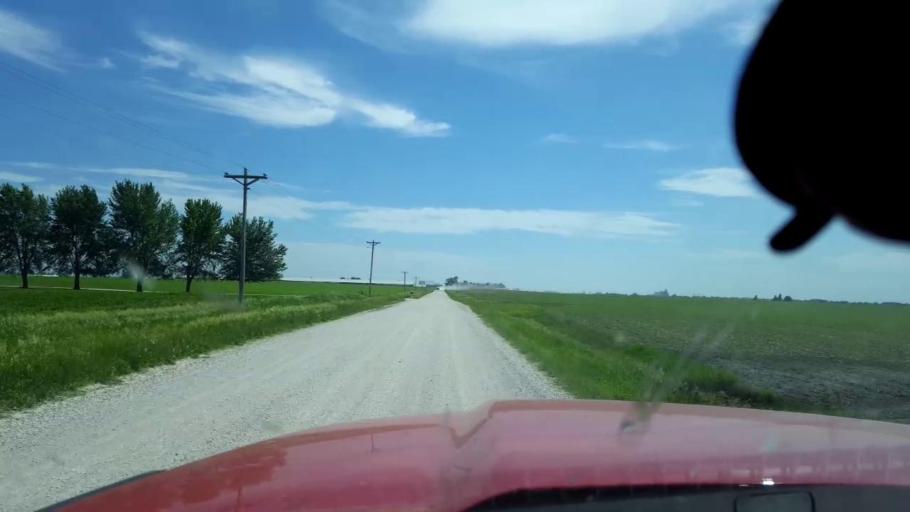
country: US
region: Iowa
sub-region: Hamilton County
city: Jewell
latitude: 42.3503
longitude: -93.5604
